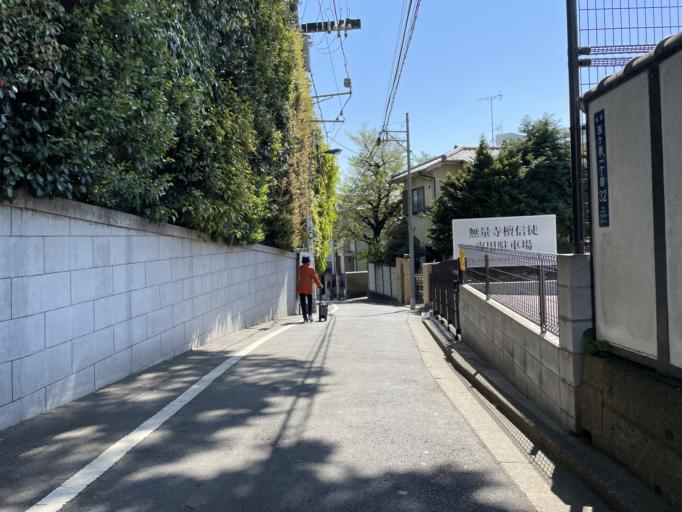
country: JP
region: Saitama
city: Kawaguchi
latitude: 35.7435
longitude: 139.7445
